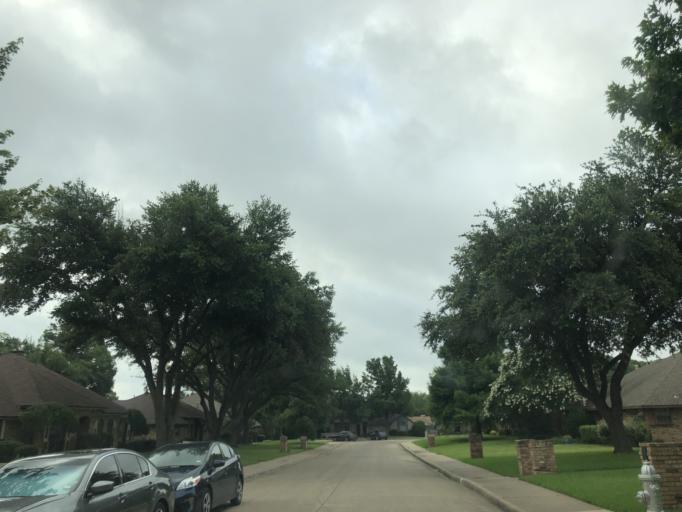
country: US
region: Texas
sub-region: Dallas County
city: Garland
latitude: 32.8368
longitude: -96.6454
